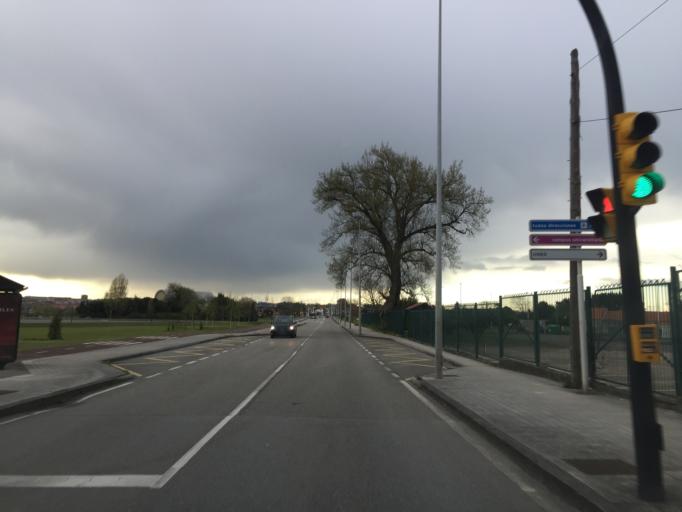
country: ES
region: Asturias
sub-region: Province of Asturias
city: Gijon
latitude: 43.5246
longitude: -5.6235
